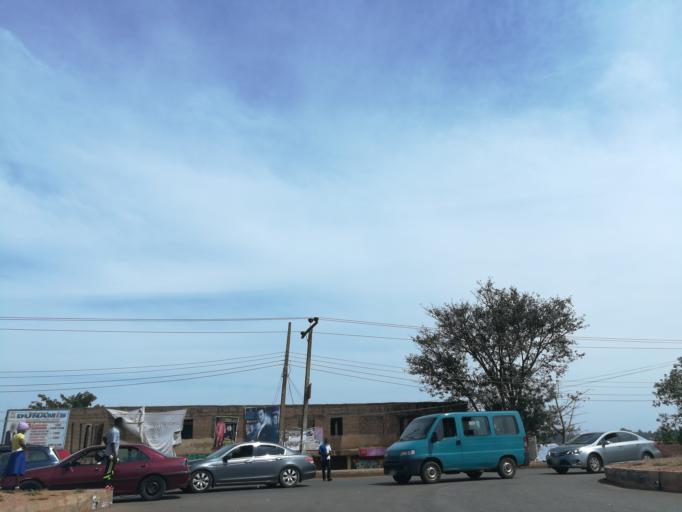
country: NG
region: Plateau
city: Bukuru
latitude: 9.7693
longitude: 8.8601
